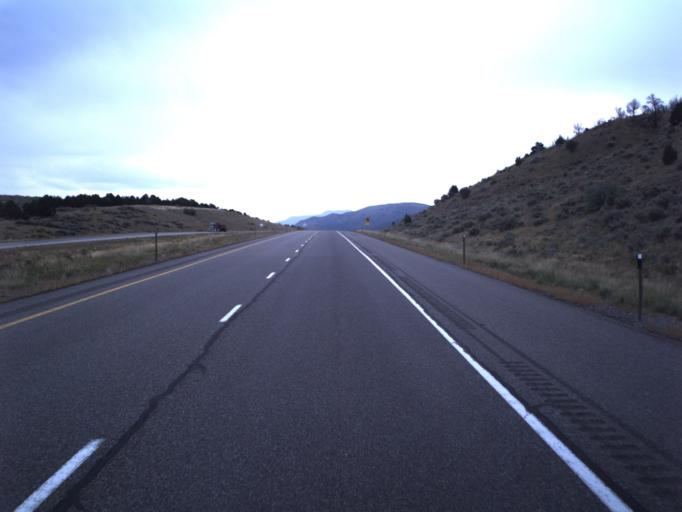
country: US
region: Utah
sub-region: Sevier County
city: Monroe
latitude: 38.5538
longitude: -112.4188
